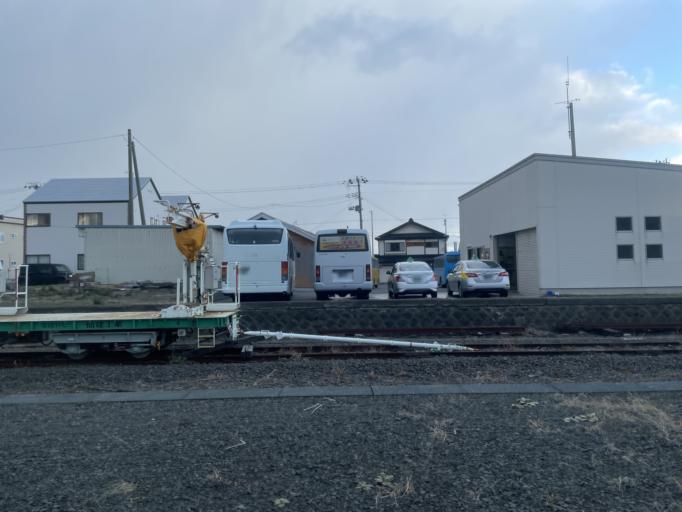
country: JP
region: Aomori
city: Mutsu
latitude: 41.0869
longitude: 141.2498
